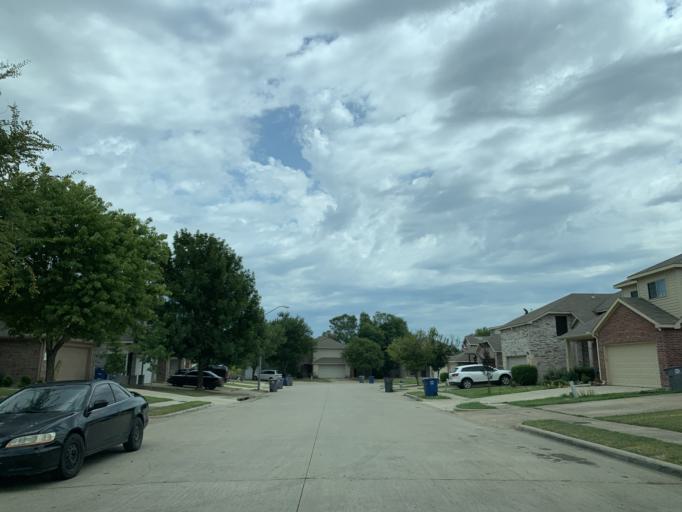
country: US
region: Texas
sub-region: Dallas County
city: DeSoto
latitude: 32.6552
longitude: -96.8199
